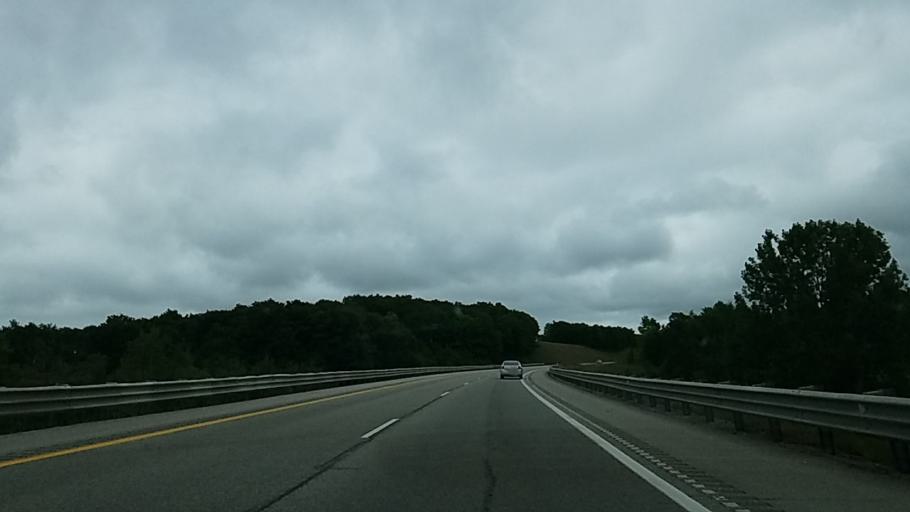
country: US
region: Michigan
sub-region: Otsego County
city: Gaylord
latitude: 45.1235
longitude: -84.6729
